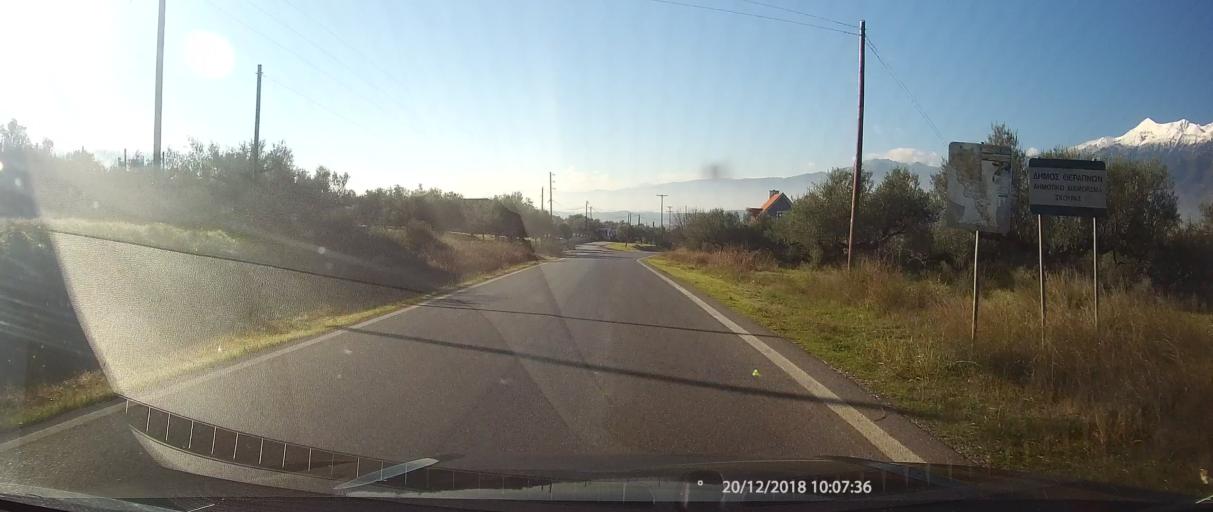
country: GR
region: Peloponnese
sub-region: Nomos Lakonias
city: Sparti
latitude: 37.0171
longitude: 22.4944
